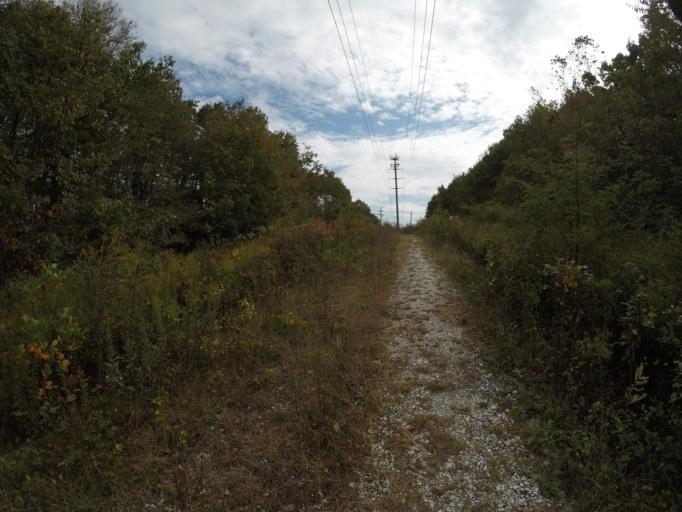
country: US
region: Maryland
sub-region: Harford County
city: Riverside
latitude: 39.4526
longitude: -76.2672
